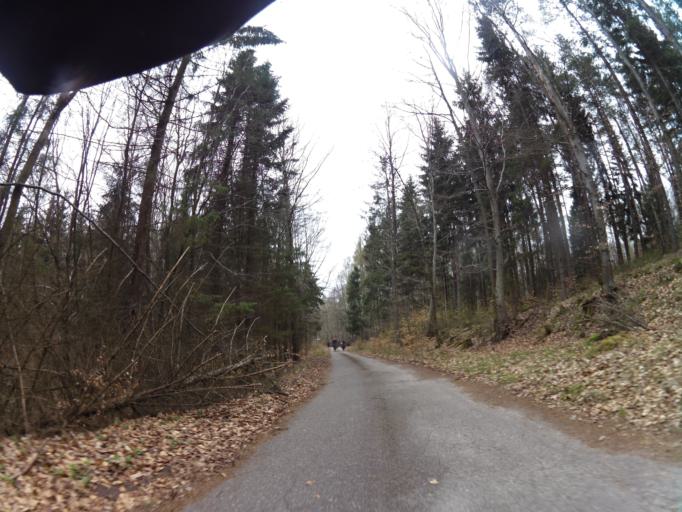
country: PL
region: West Pomeranian Voivodeship
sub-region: Powiat koszalinski
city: Bobolice
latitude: 53.9451
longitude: 16.6851
